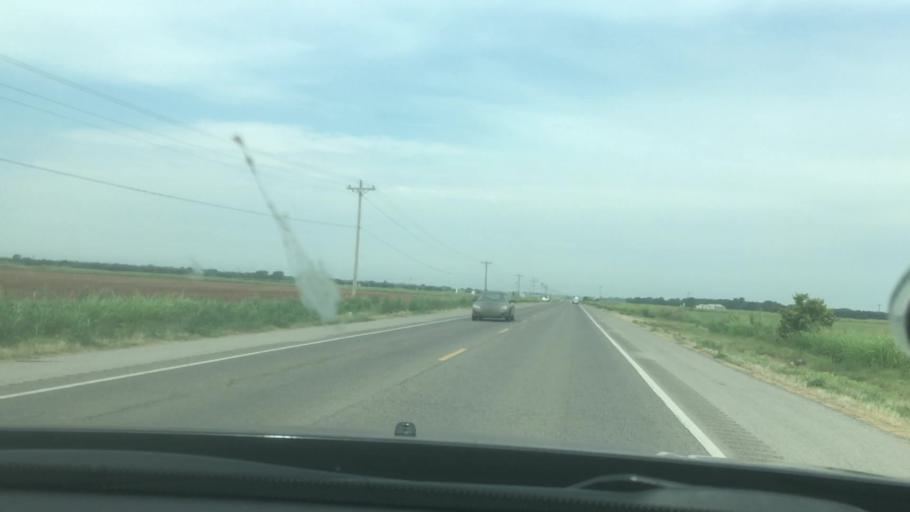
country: US
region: Oklahoma
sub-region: Garvin County
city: Lindsay
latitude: 34.8217
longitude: -97.5051
